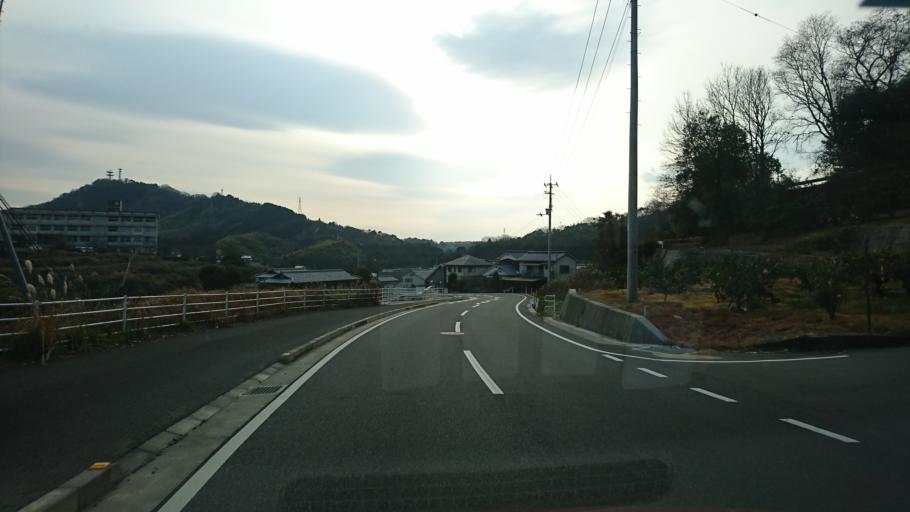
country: JP
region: Ehime
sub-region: Shikoku-chuo Shi
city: Matsuyama
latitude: 33.8807
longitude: 132.8022
